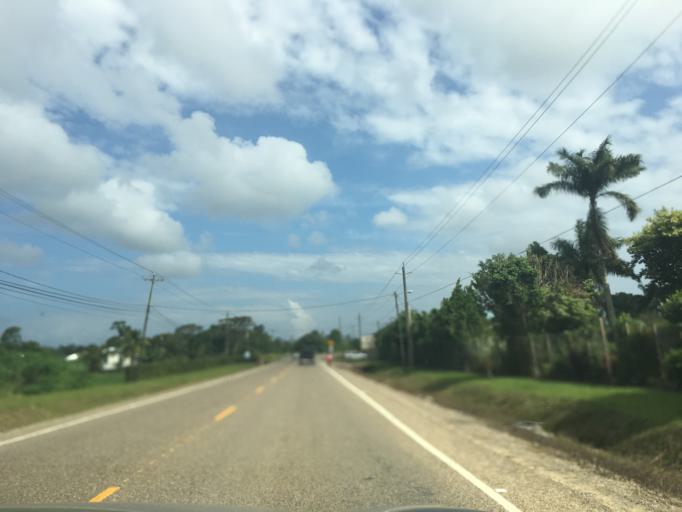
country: BZ
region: Stann Creek
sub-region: Dangriga
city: Dangriga
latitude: 17.0014
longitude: -88.3100
